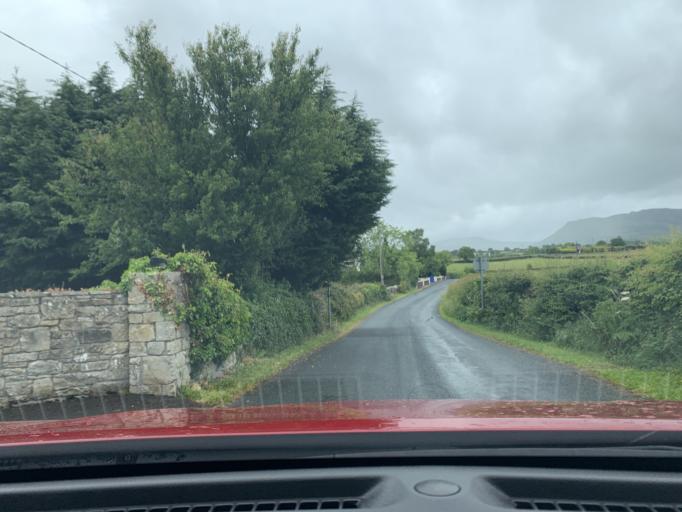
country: IE
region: Connaught
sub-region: Sligo
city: Sligo
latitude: 54.2944
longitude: -8.4630
